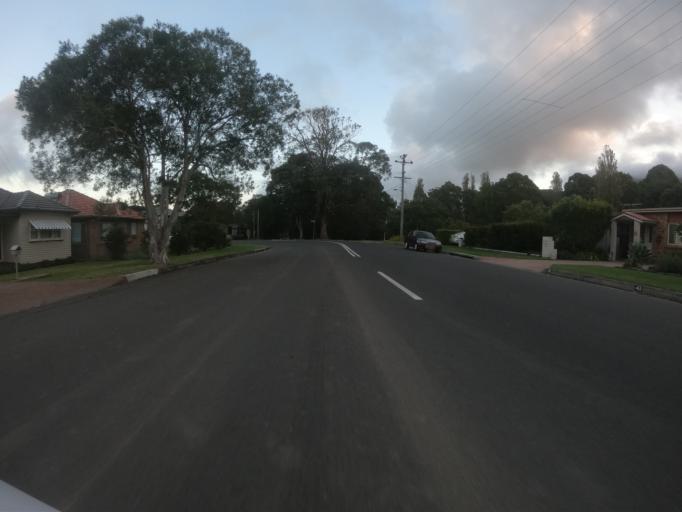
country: AU
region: New South Wales
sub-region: Wollongong
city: Mount Ousley
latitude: -34.3941
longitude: 150.8788
